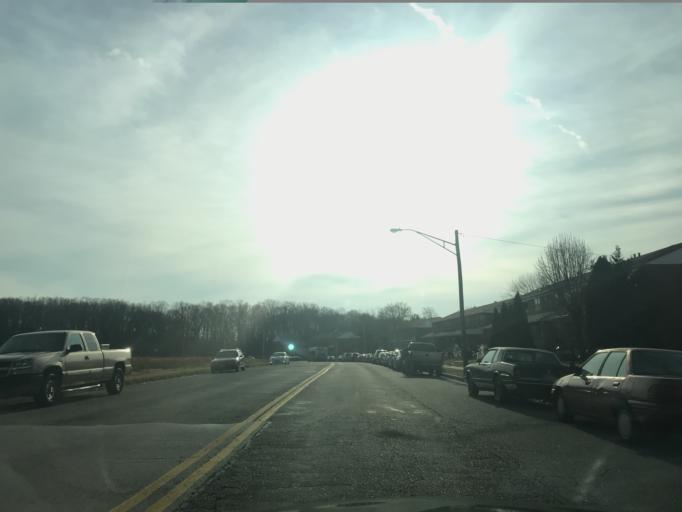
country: US
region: Maryland
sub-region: Baltimore County
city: Essex
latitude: 39.2959
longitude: -76.4501
